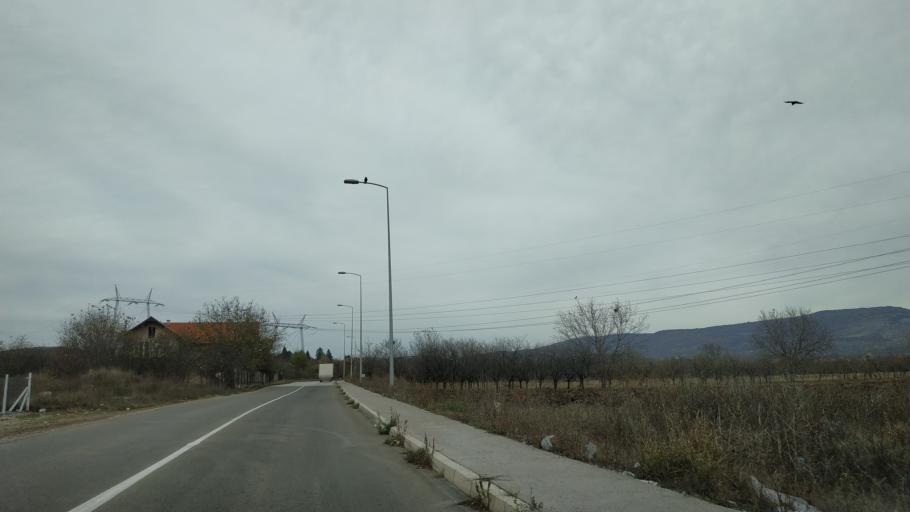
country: RS
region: Central Serbia
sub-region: Nisavski Okrug
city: Nis
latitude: 43.3438
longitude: 21.9370
